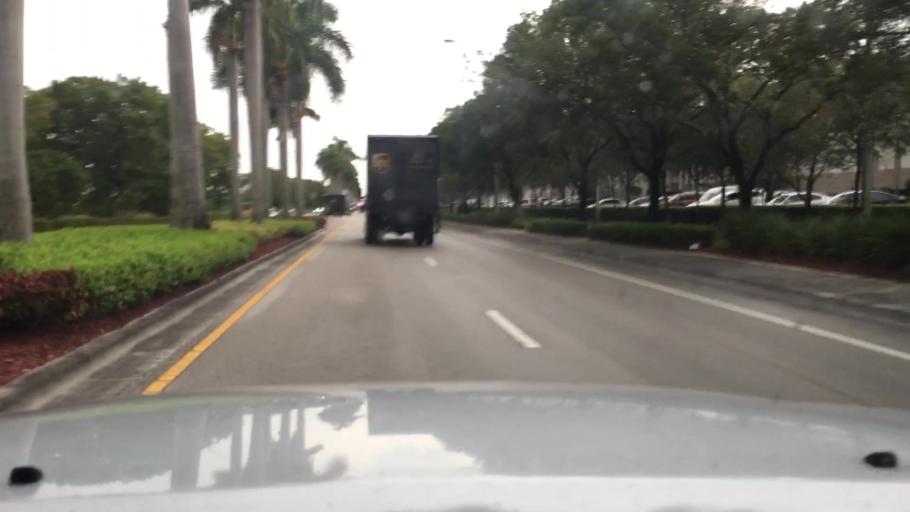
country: US
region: Florida
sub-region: Miami-Dade County
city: Tamiami
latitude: 25.7967
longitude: -80.3944
